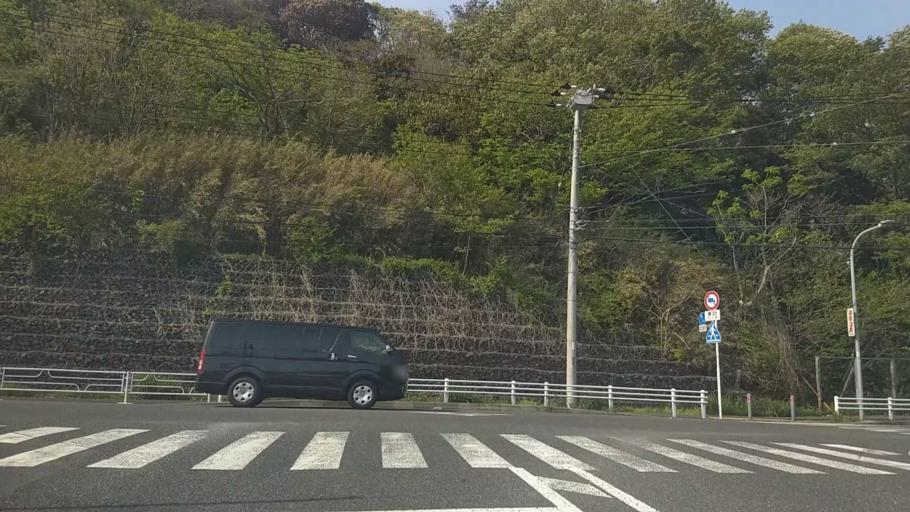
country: JP
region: Kanagawa
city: Kamakura
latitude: 35.3836
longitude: 139.5539
